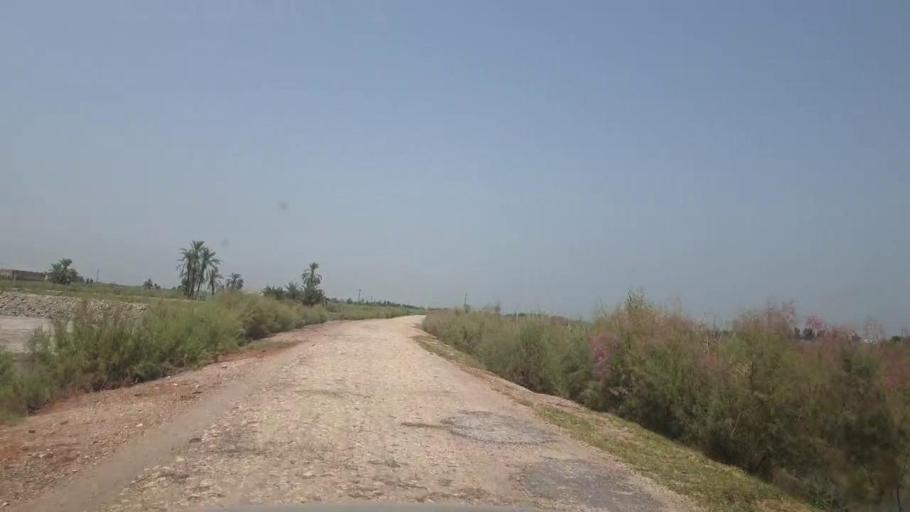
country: PK
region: Sindh
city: Lakhi
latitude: 27.8453
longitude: 68.6257
